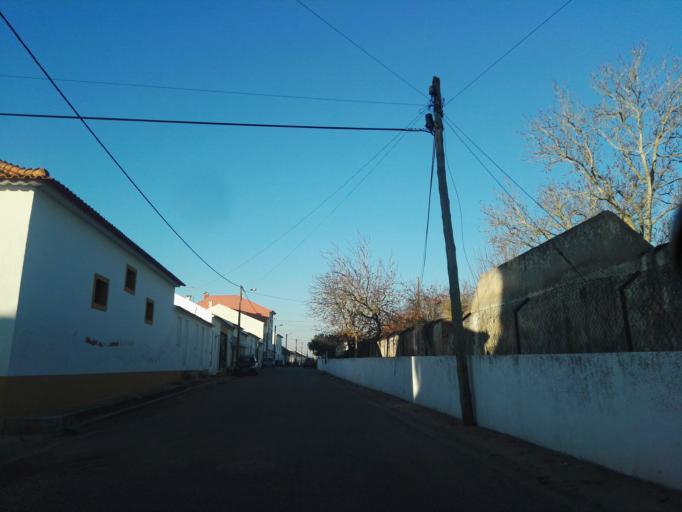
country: PT
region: Santarem
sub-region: Golega
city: Golega
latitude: 39.3440
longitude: -8.5511
